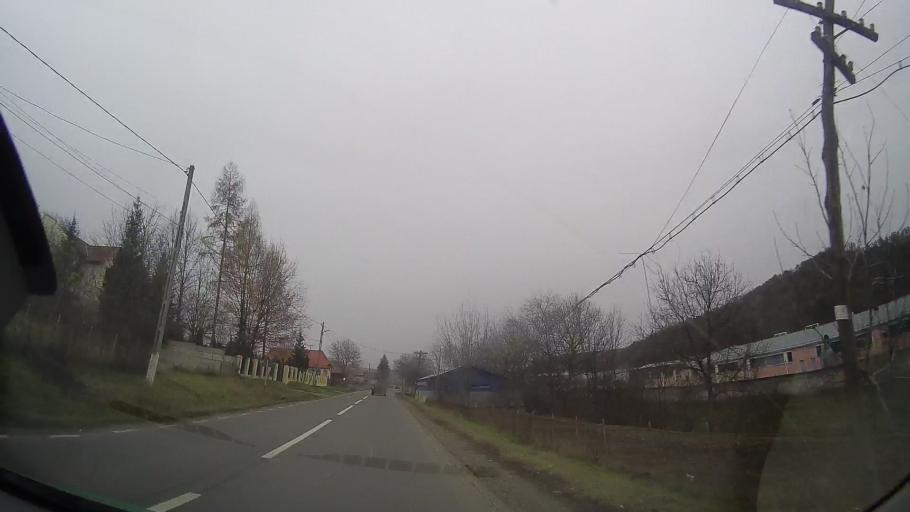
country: RO
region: Mures
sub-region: Comuna Ceausu de Campie
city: Ceausu de Campie
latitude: 46.6182
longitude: 24.5255
